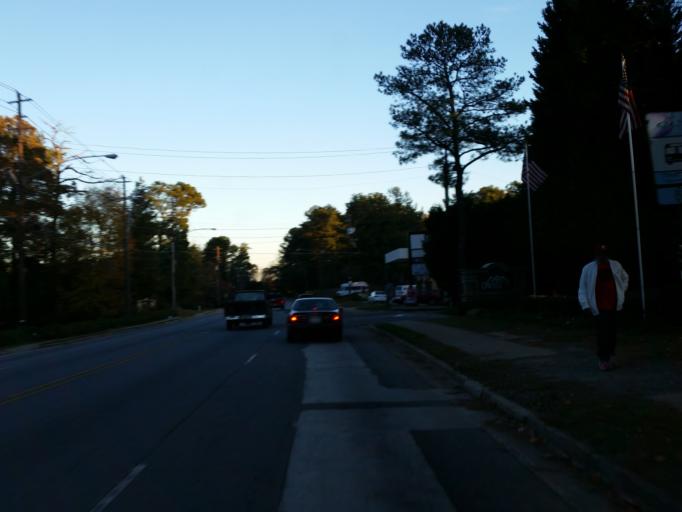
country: US
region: Georgia
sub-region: Cobb County
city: Fair Oaks
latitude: 33.9332
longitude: -84.5016
